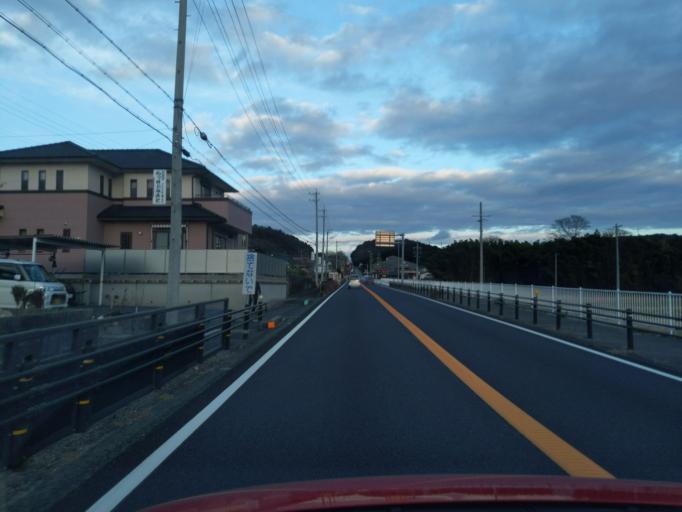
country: JP
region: Gifu
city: Mizunami
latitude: 35.4014
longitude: 137.2864
